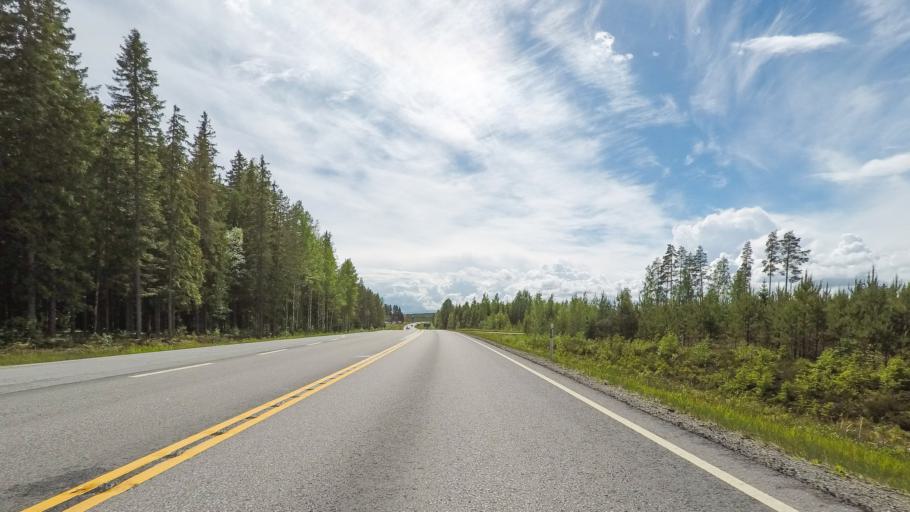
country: FI
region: Central Finland
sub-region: Jyvaeskylae
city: Hankasalmi
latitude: 62.3637
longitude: 26.5728
